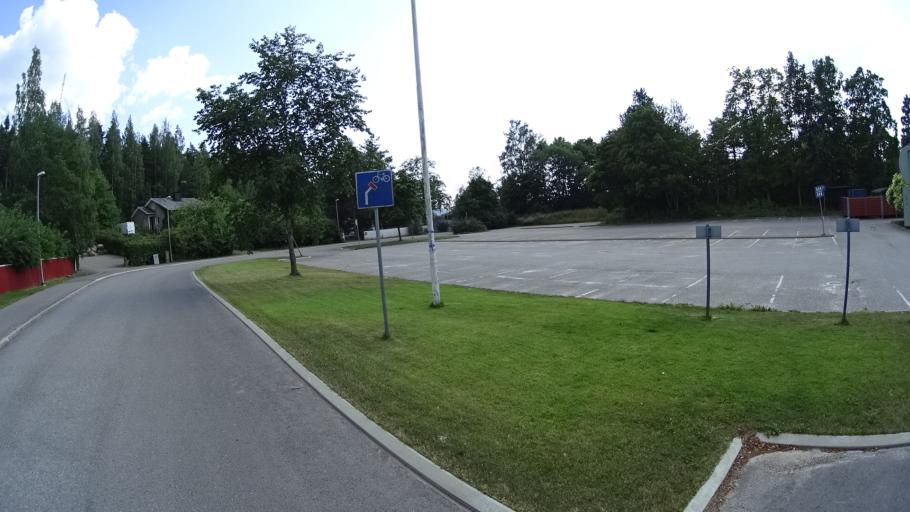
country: FI
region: Uusimaa
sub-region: Porvoo
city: Porvoo
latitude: 60.3886
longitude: 25.6736
